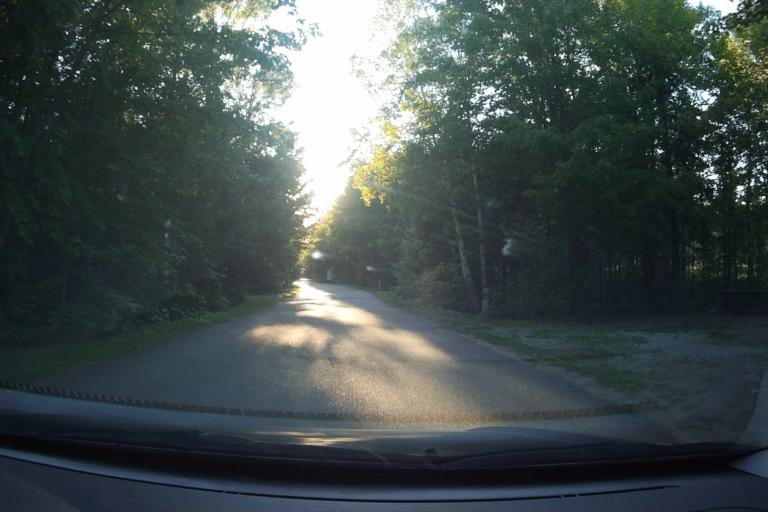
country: CA
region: Ontario
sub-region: Algoma
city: Sault Ste. Marie
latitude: 46.9699
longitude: -84.6912
